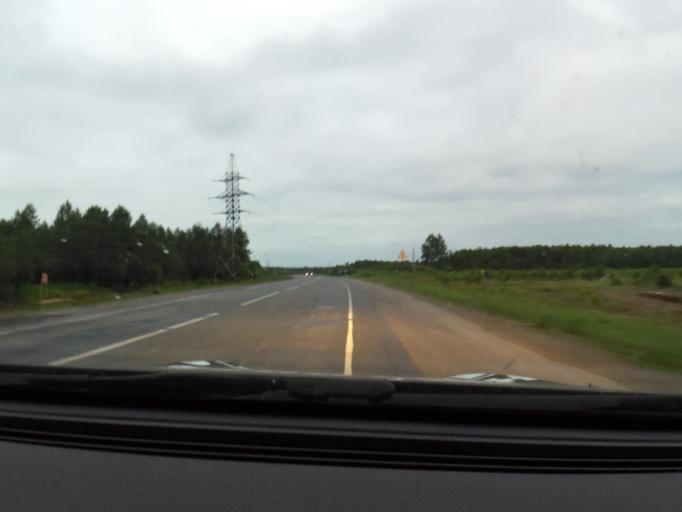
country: RU
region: Perm
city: Krasnokamsk
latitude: 58.0934
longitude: 55.7318
